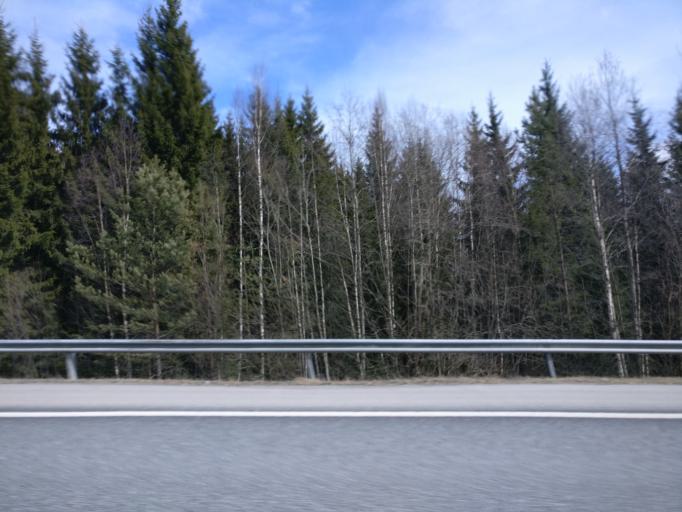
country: FI
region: Haeme
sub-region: Haemeenlinna
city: Haemeenlinna
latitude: 60.9406
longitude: 24.5132
